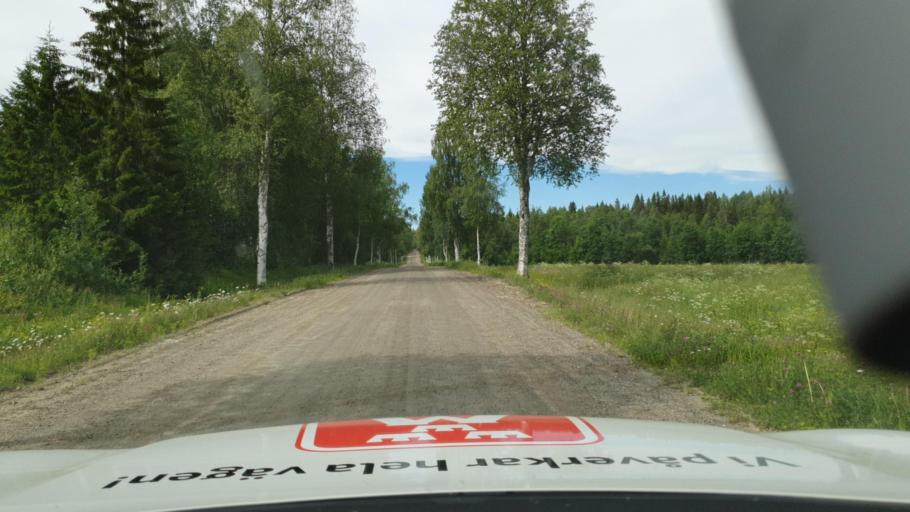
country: SE
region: Vaesterbotten
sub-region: Skelleftea Kommun
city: Burtraesk
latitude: 64.4695
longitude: 20.4575
